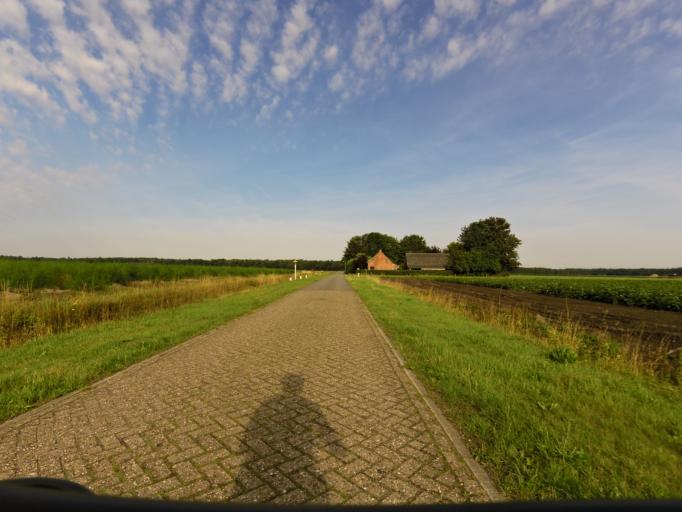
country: NL
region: North Brabant
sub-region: Gemeente Woensdrecht
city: Woensdrecht
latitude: 51.4478
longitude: 4.3794
